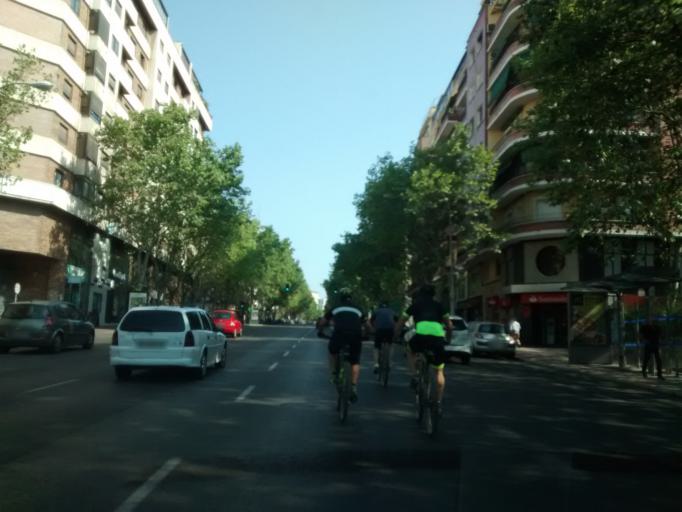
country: ES
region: Madrid
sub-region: Provincia de Madrid
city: Arganzuela
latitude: 40.4021
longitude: -3.6938
